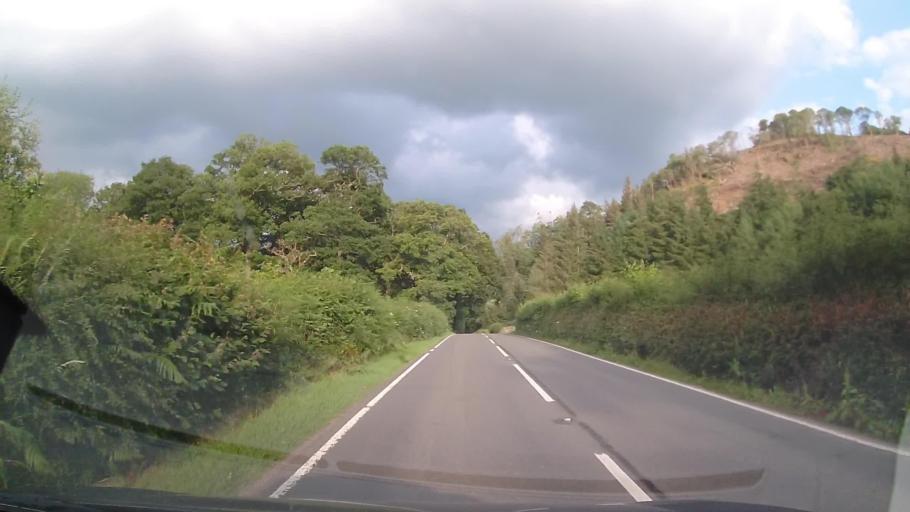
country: GB
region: Wales
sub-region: Gwynedd
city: Bala
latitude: 52.9092
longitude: -3.5418
